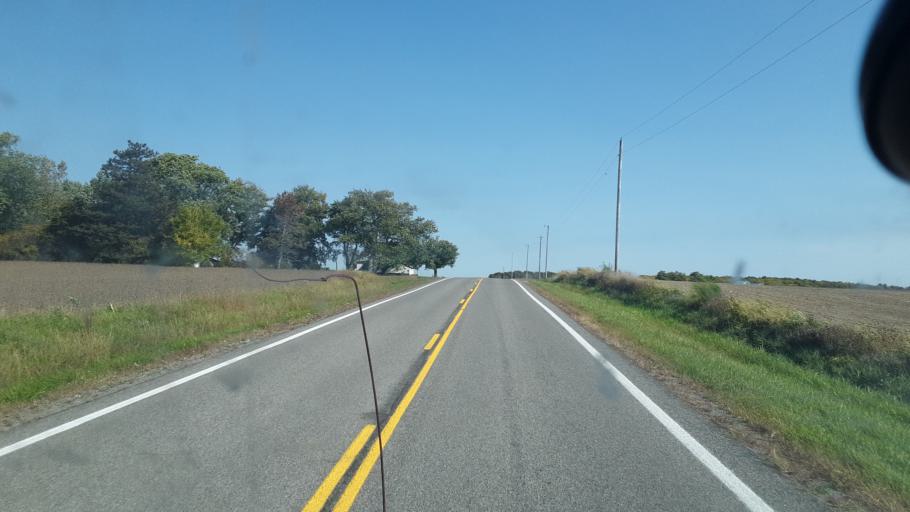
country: US
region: Ohio
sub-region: Logan County
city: Northwood
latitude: 40.5072
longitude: -83.6618
